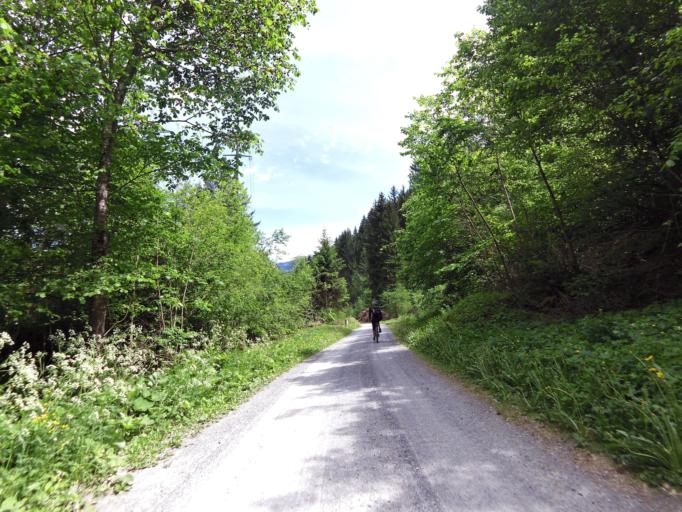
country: CH
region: Grisons
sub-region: Surselva District
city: Ilanz
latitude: 46.7733
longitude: 9.1662
